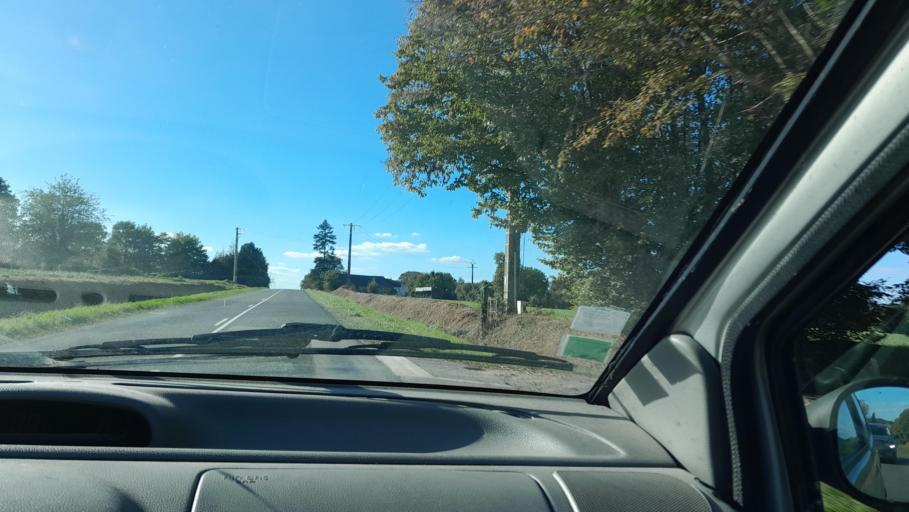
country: FR
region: Pays de la Loire
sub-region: Departement de la Mayenne
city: Cosse-le-Vivien
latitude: 47.9549
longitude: -0.9441
